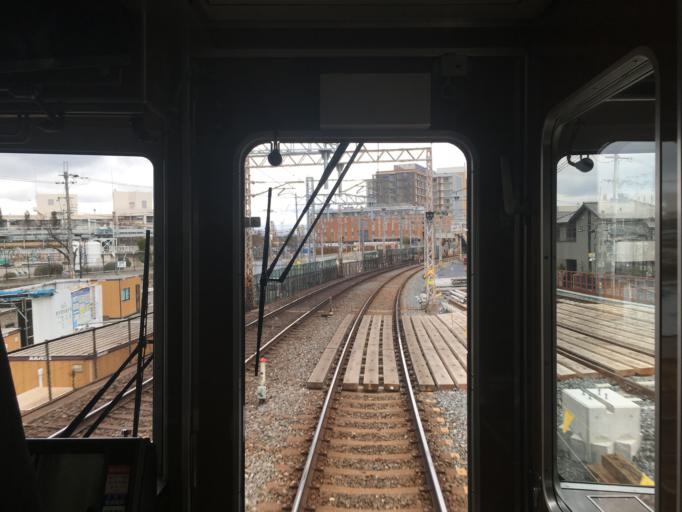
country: JP
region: Osaka
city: Suita
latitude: 34.7273
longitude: 135.5107
